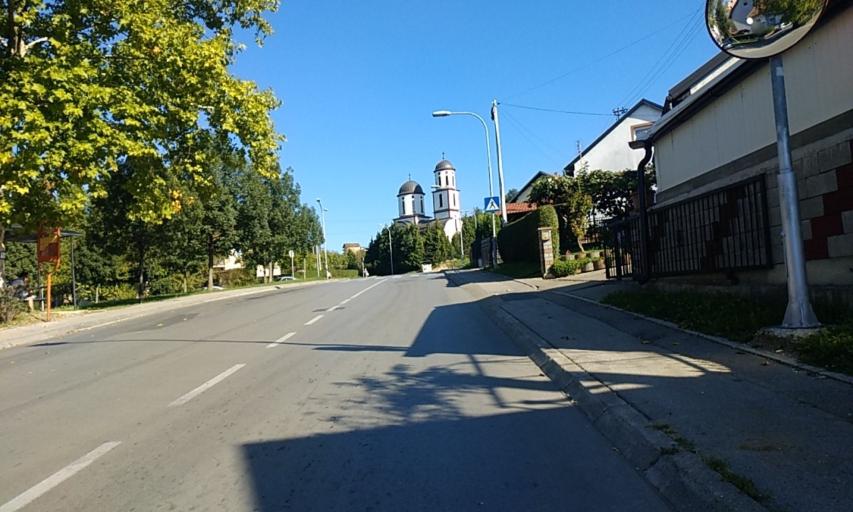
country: BA
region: Republika Srpska
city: Starcevica
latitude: 44.7567
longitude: 17.2085
